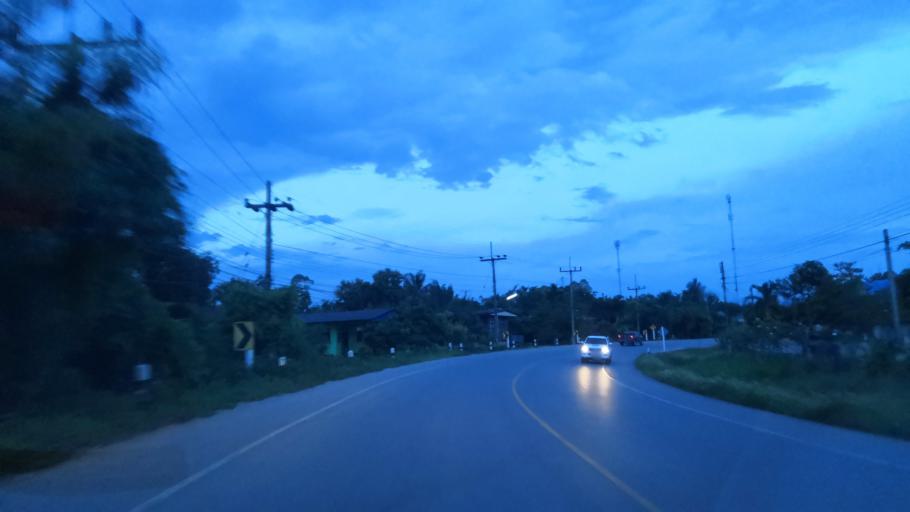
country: TH
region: Chiang Rai
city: Wiang Chiang Rung
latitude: 19.9646
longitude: 100.0069
